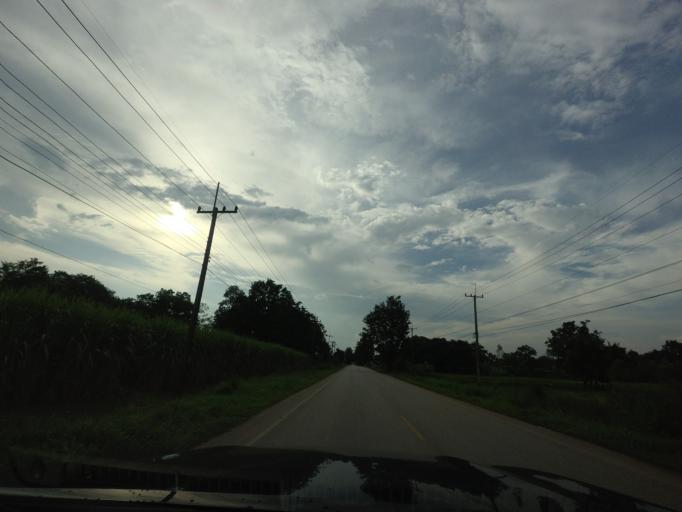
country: TH
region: Changwat Udon Thani
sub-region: Amphoe Ban Phue
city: Ban Phue
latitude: 17.7100
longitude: 102.4196
